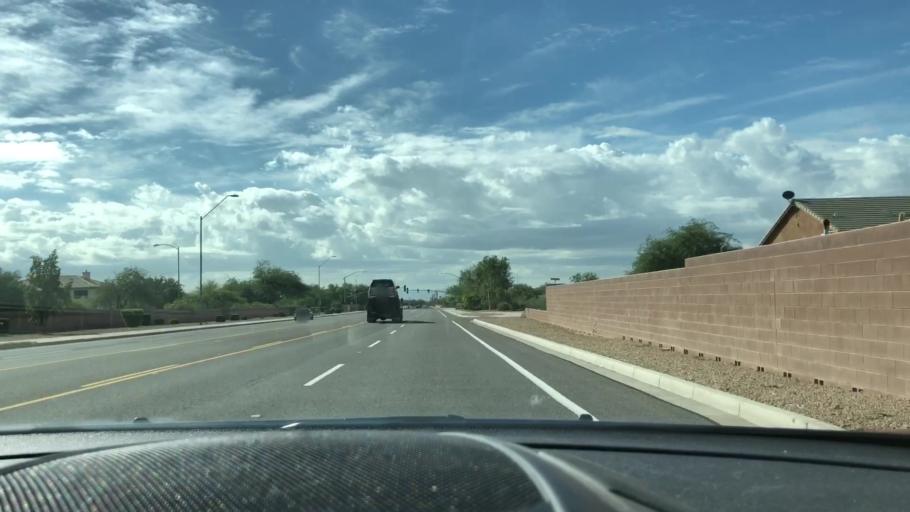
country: US
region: Arizona
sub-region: Maricopa County
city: Sun City
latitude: 33.6986
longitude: -112.2378
